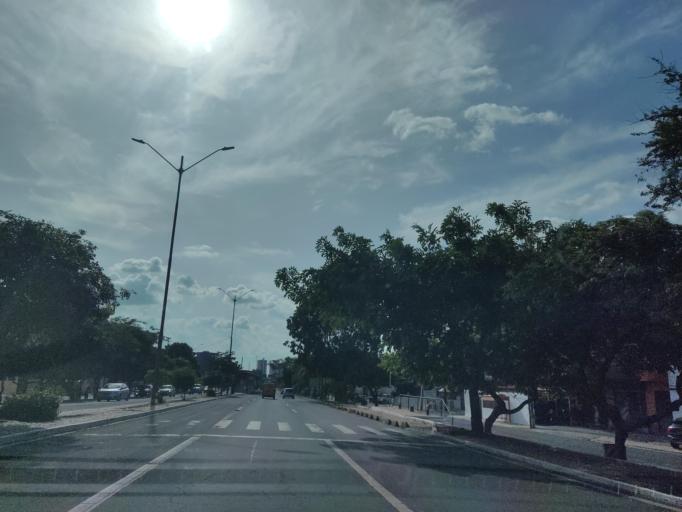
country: BR
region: Piaui
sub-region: Teresina
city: Teresina
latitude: -5.0808
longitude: -42.7762
